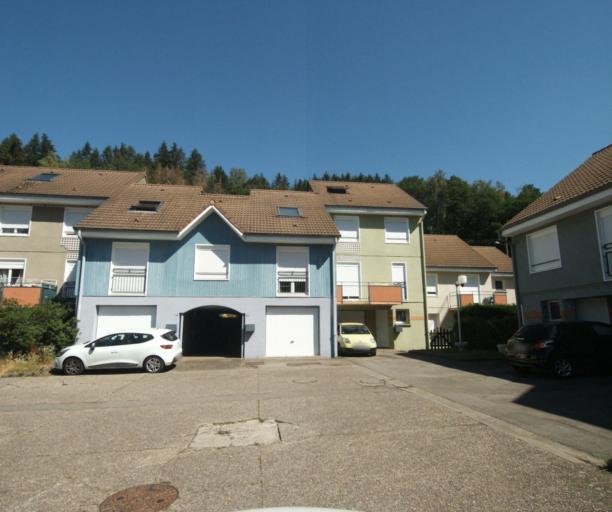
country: FR
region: Lorraine
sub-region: Departement des Vosges
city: Epinal
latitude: 48.1632
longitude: 6.4630
